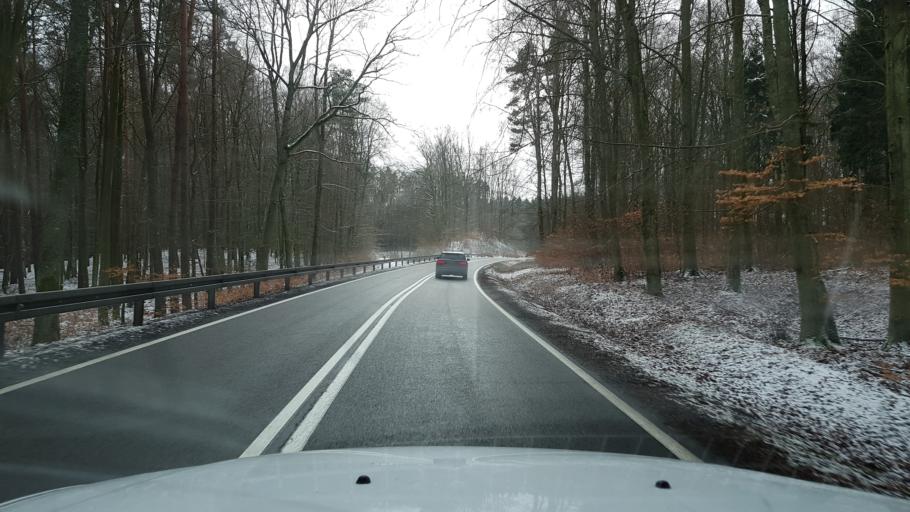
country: PL
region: West Pomeranian Voivodeship
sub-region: Powiat drawski
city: Wierzchowo
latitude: 53.5397
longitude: 16.0981
